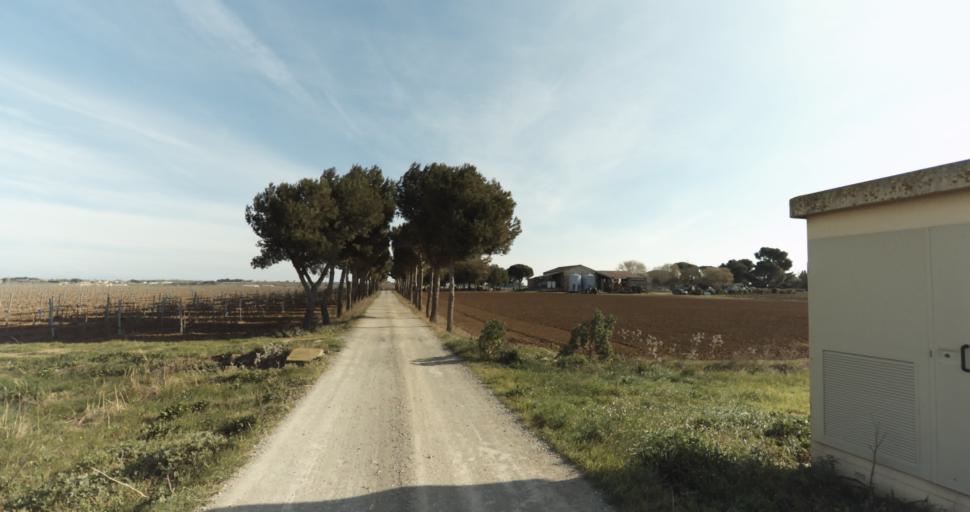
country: FR
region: Languedoc-Roussillon
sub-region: Departement de l'Herault
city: Pomerols
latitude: 43.3712
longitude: 3.5044
